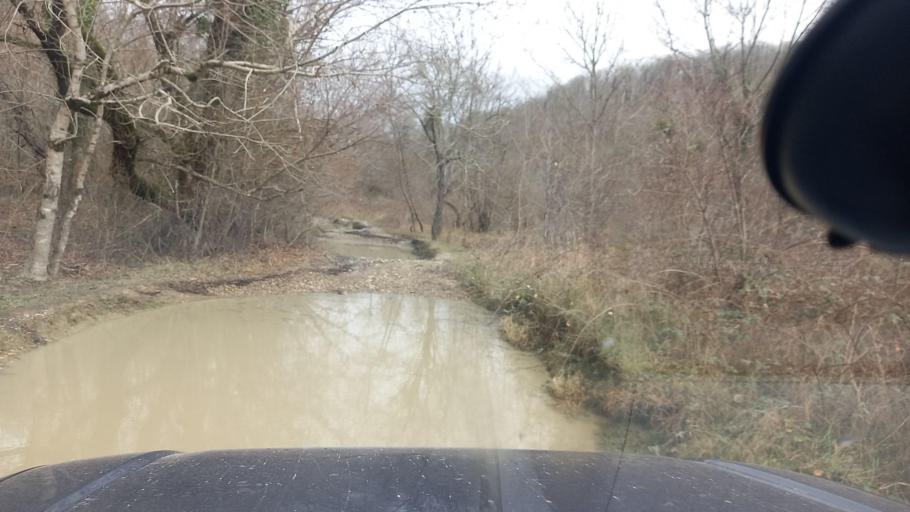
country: RU
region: Krasnodarskiy
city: Pshada
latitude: 44.4843
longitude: 38.4091
